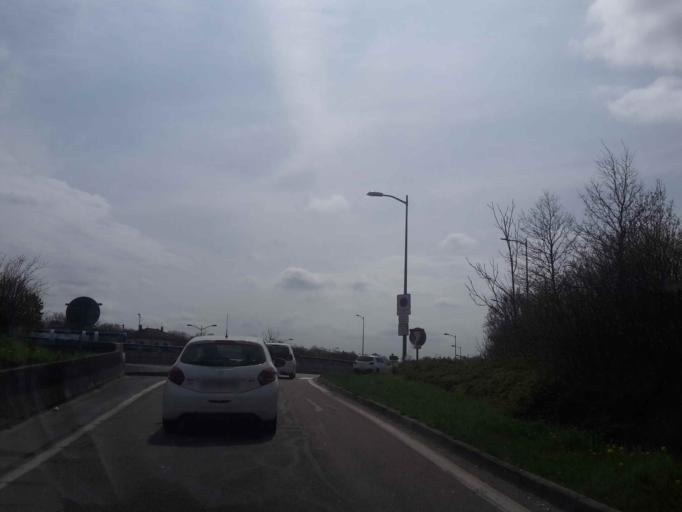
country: FR
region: Franche-Comte
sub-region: Departement du Doubs
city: Besancon
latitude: 47.2627
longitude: 6.0052
